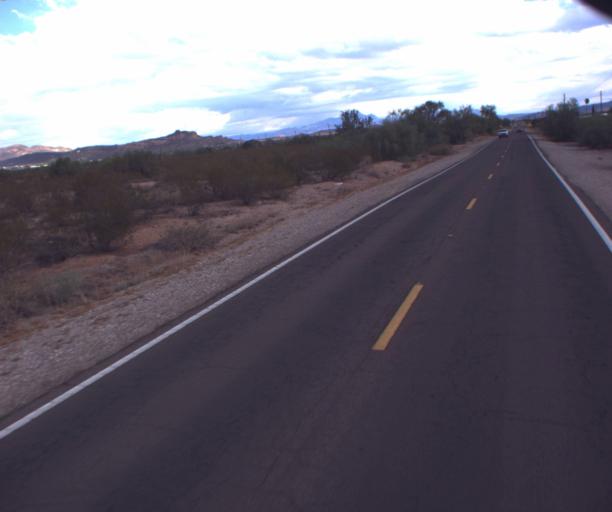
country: US
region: Arizona
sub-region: Pinal County
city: Apache Junction
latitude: 33.4288
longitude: -111.5325
